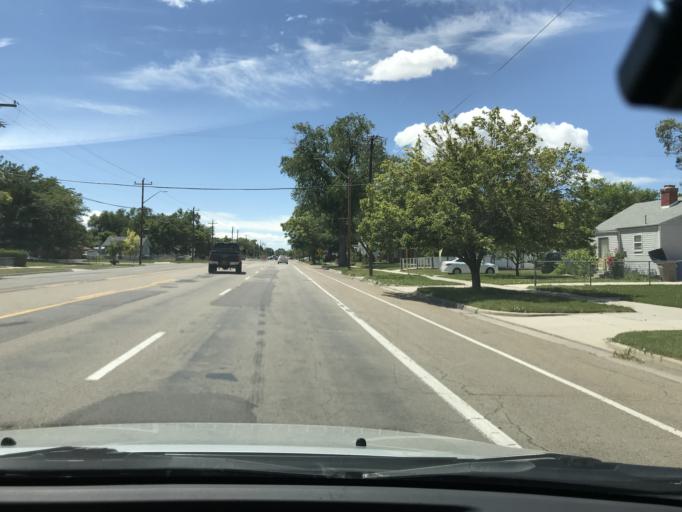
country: US
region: Utah
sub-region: Salt Lake County
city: Salt Lake City
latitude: 40.7825
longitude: -111.9214
